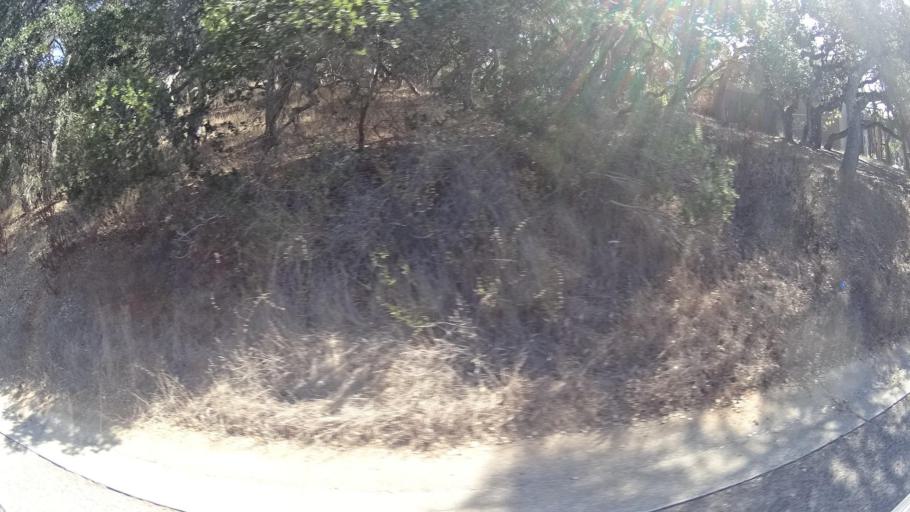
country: US
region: California
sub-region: Monterey County
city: Prunedale
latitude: 36.8046
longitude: -121.6297
